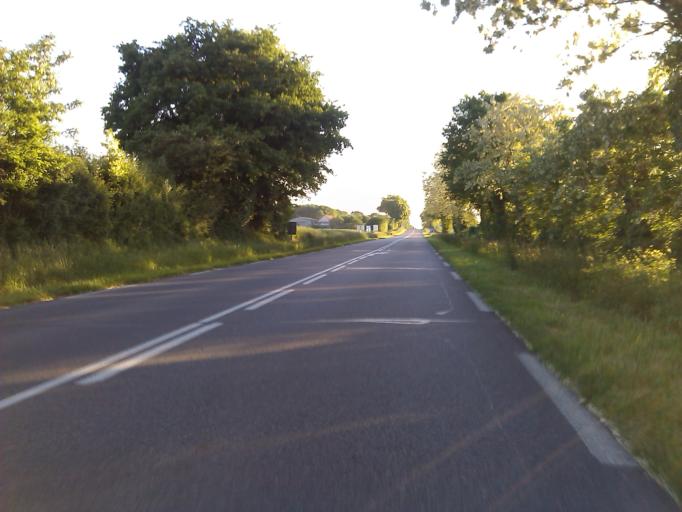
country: FR
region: Poitou-Charentes
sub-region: Departement de la Vienne
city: Saint-Savin
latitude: 46.5893
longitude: 0.9432
